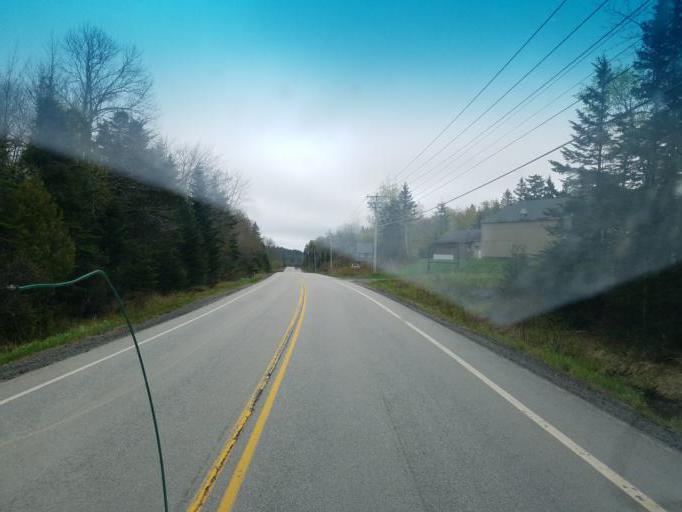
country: US
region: Maine
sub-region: Washington County
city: Eastport
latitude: 44.8048
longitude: -67.1010
